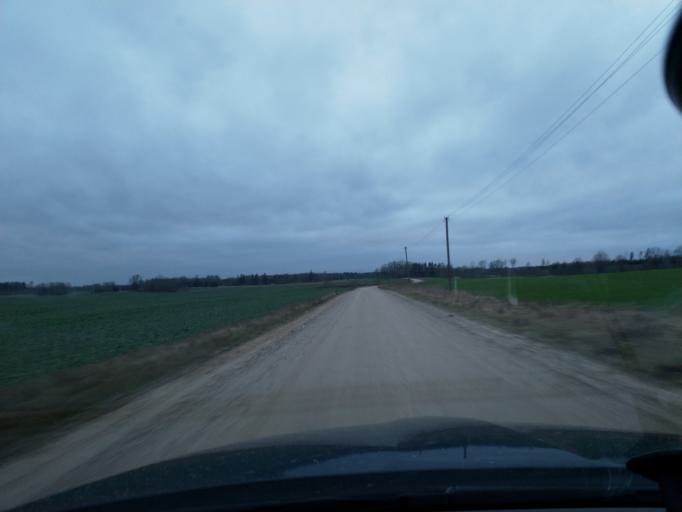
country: LV
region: Saldus Rajons
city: Saldus
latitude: 56.8962
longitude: 22.3178
